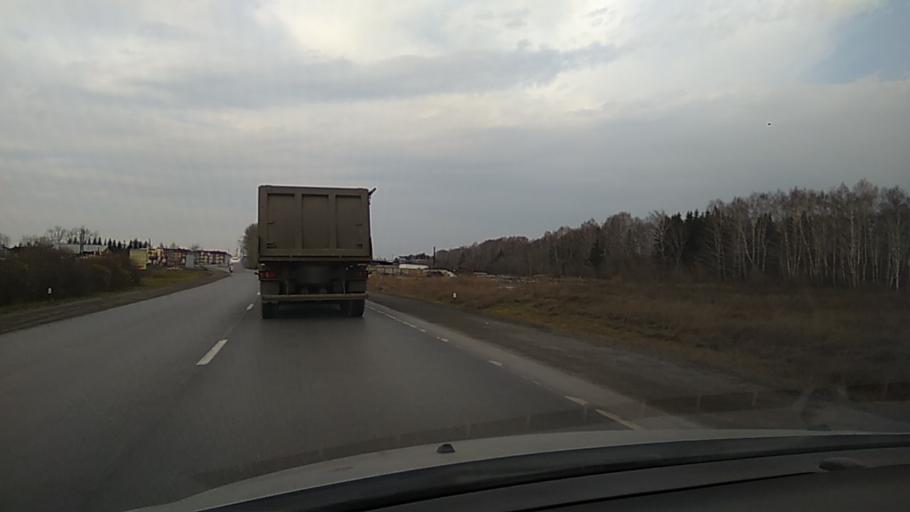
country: RU
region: Sverdlovsk
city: Tugulym
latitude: 57.0678
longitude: 64.6613
